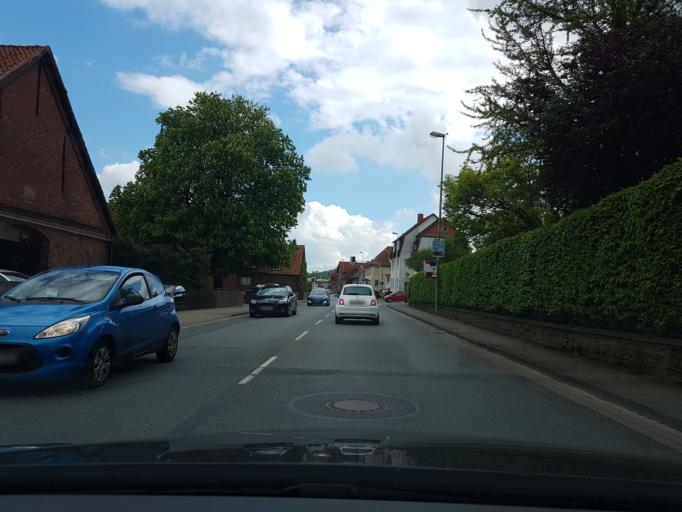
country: DE
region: Lower Saxony
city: Hameln
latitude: 52.1001
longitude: 9.4120
